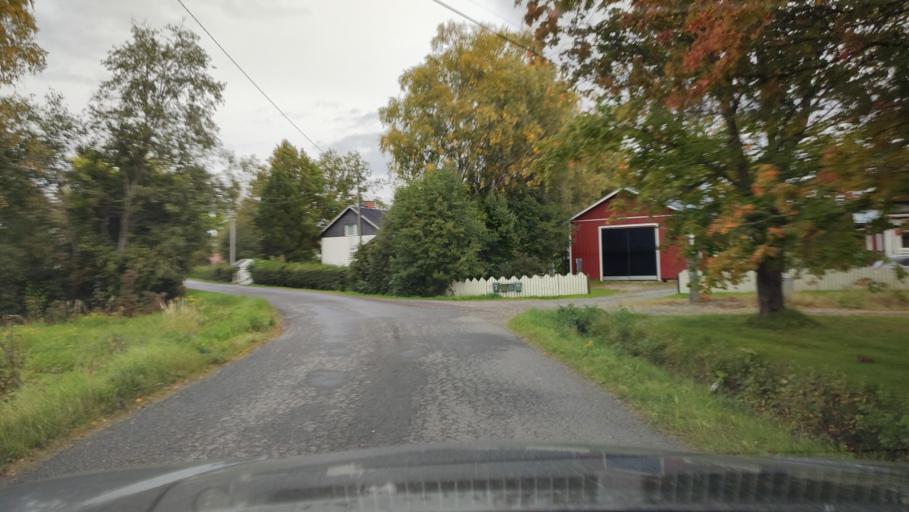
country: FI
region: Ostrobothnia
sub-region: Sydosterbotten
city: Kristinestad
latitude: 62.2544
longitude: 21.5000
